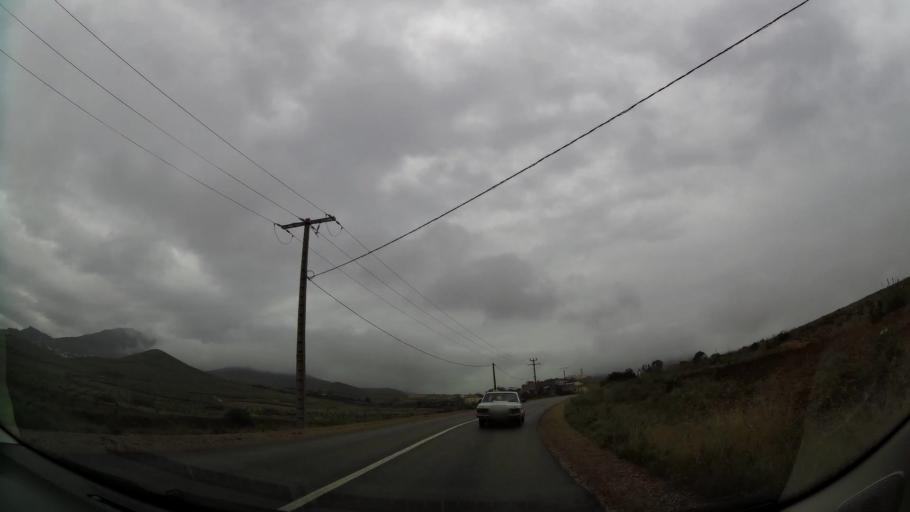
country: MA
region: Oriental
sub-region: Nador
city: Nador
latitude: 35.1473
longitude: -3.0407
